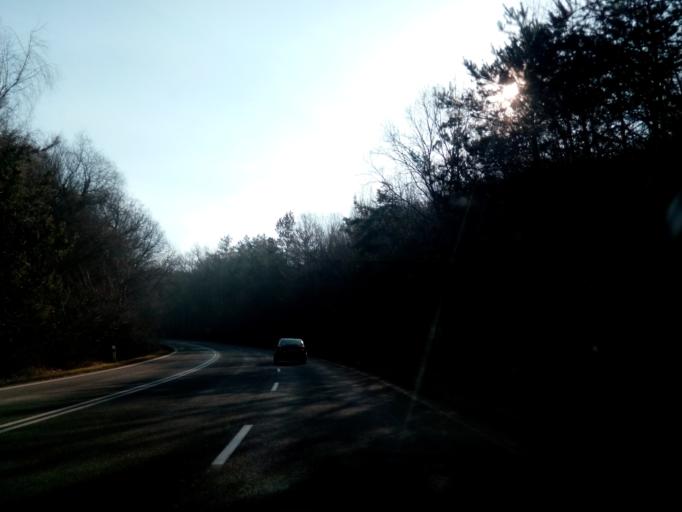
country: SK
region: Kosicky
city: Kosice
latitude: 48.7359
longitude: 21.3713
